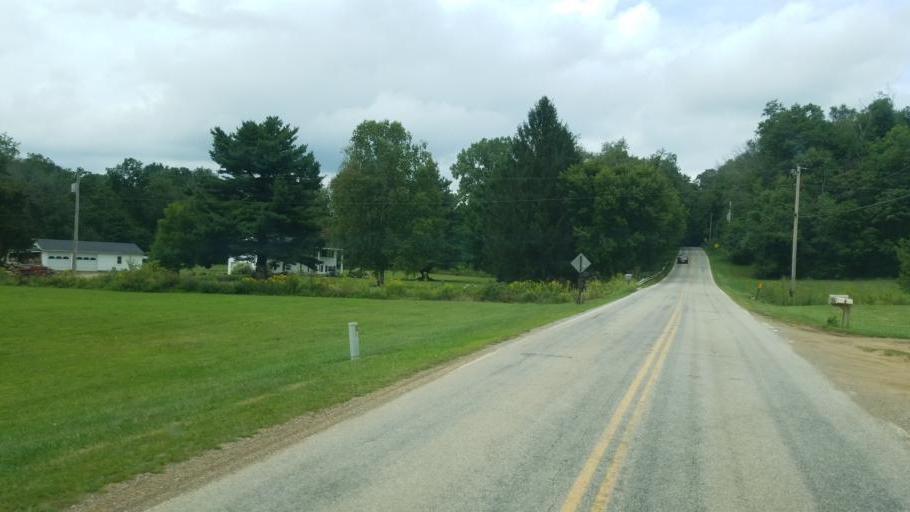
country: US
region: Ohio
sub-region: Sandusky County
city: Bellville
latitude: 40.6440
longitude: -82.4701
